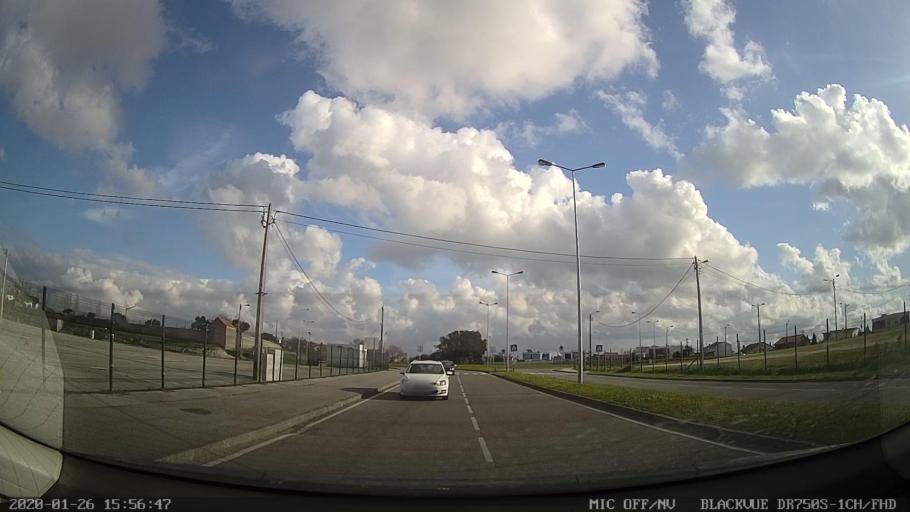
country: PT
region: Aveiro
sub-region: Aveiro
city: Aradas
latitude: 40.6326
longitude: -8.6303
